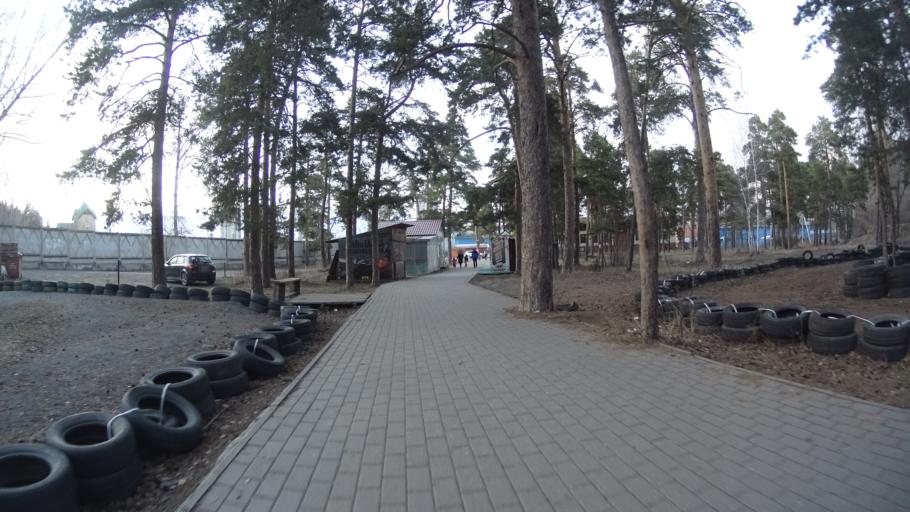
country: RU
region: Chelyabinsk
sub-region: Gorod Chelyabinsk
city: Chelyabinsk
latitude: 55.1666
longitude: 61.3701
